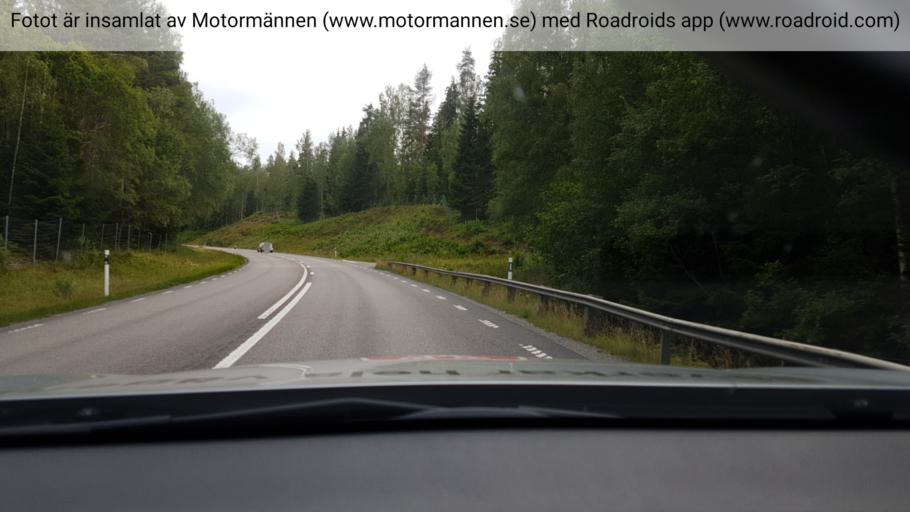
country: SE
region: Vaestra Goetaland
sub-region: Bengtsfors Kommun
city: Billingsfors
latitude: 59.0046
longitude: 12.2688
